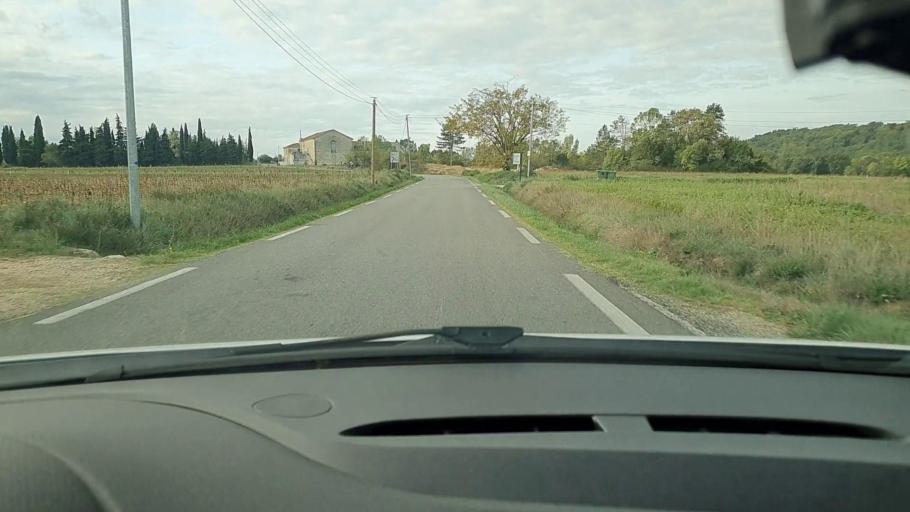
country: FR
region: Languedoc-Roussillon
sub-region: Departement du Gard
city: Salindres
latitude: 44.1872
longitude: 4.2355
